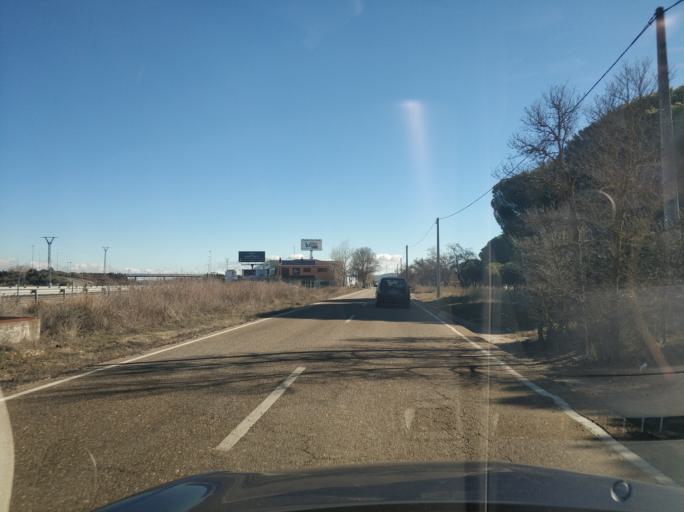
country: ES
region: Castille and Leon
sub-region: Provincia de Valladolid
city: Tudela de Duero
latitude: 41.5907
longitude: -4.6028
